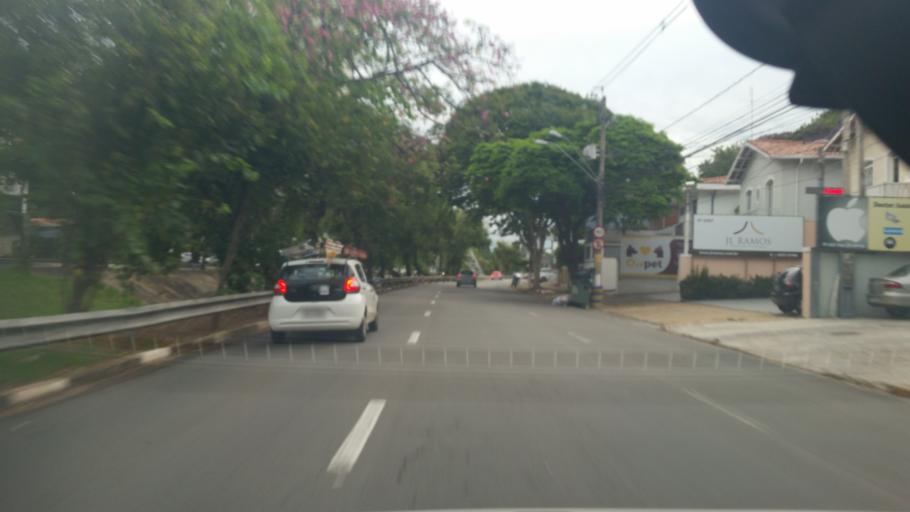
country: BR
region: Sao Paulo
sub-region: Campinas
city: Campinas
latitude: -22.8876
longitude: -47.0513
